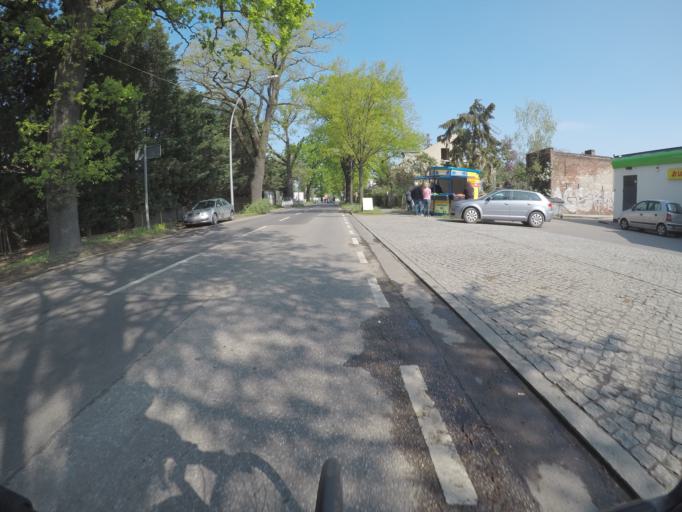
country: DE
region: Berlin
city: Buchholz
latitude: 52.6132
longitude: 13.4330
